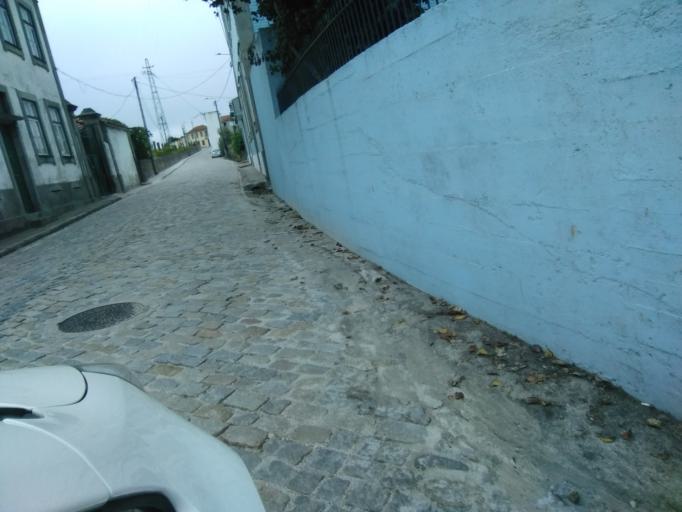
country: PT
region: Porto
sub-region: Matosinhos
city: Santa Cruz do Bispo
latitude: 41.2265
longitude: -8.7047
